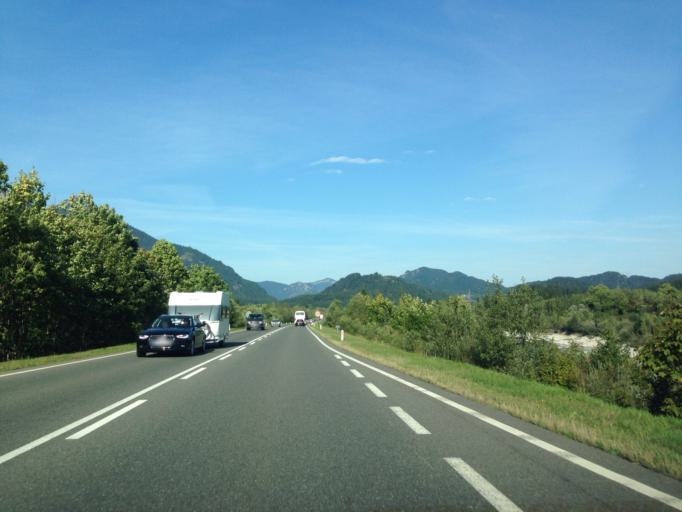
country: AT
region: Tyrol
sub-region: Politischer Bezirk Reutte
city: Pflach
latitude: 47.5263
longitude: 10.6975
